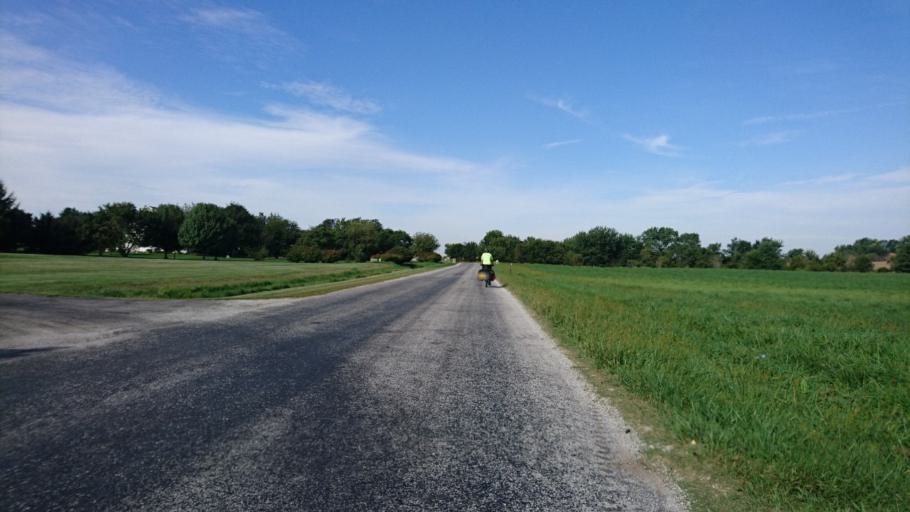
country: US
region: Illinois
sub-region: Will County
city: Manhattan
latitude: 41.4206
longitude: -88.0149
